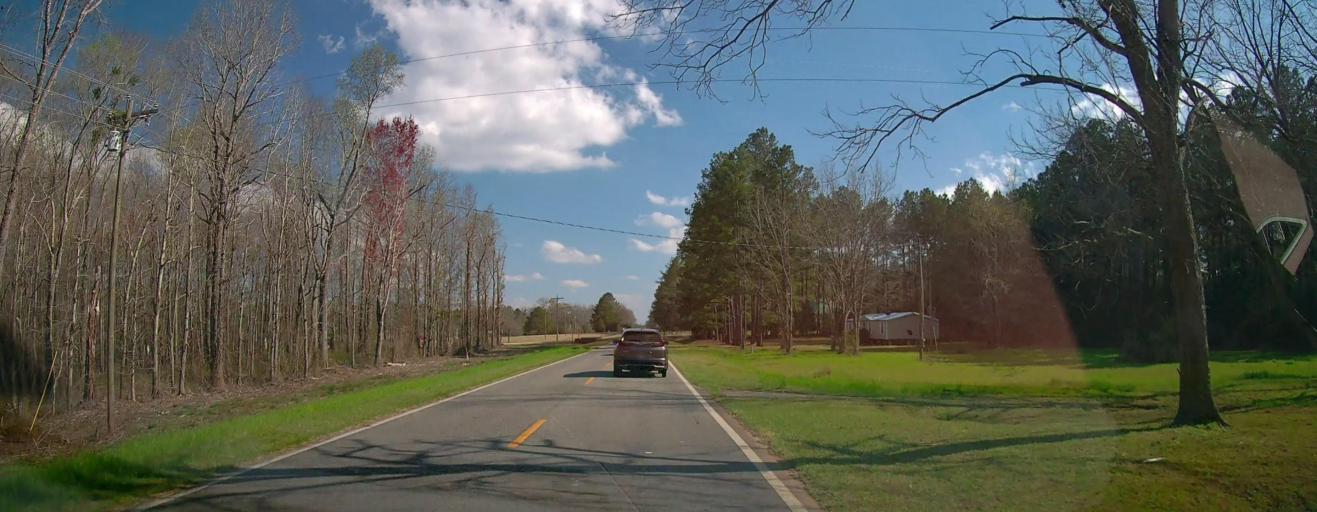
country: US
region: Georgia
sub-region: Laurens County
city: Dublin
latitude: 32.6144
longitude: -83.0834
